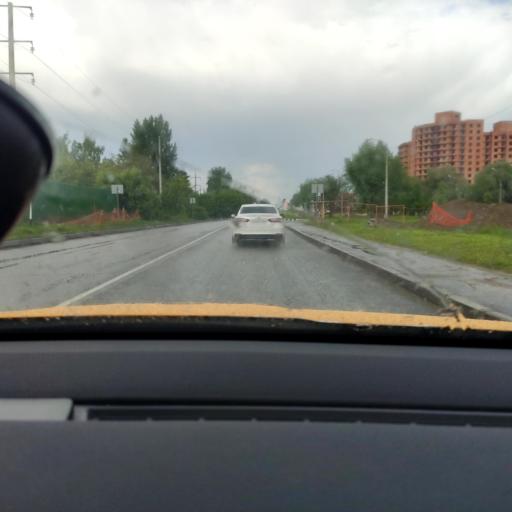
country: RU
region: Moskovskaya
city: Stupino
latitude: 54.8933
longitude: 38.0608
